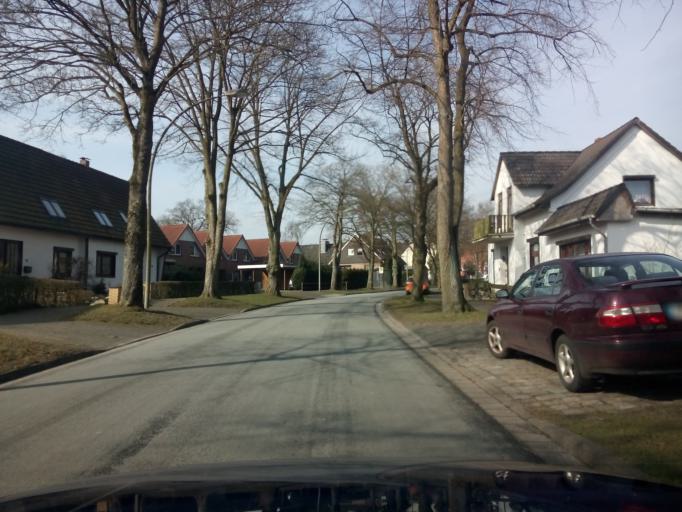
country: DE
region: Lower Saxony
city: Ritterhude
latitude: 53.1795
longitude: 8.7430
